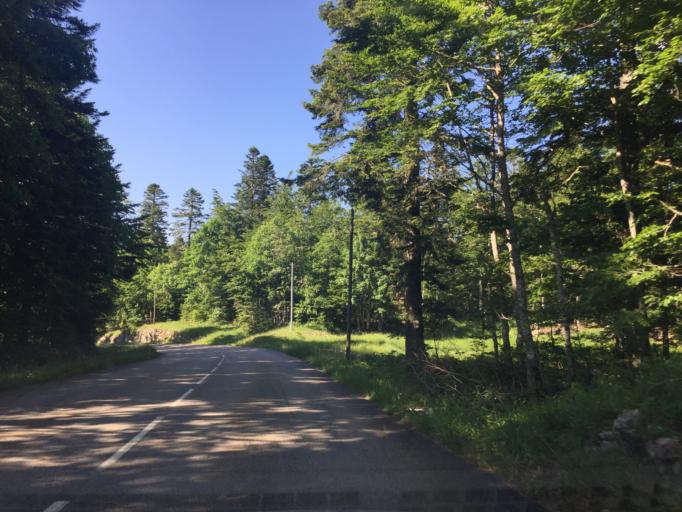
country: FR
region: Rhone-Alpes
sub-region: Departement de la Drome
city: Saint-Jean-en-Royans
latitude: 44.9186
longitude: 5.3253
